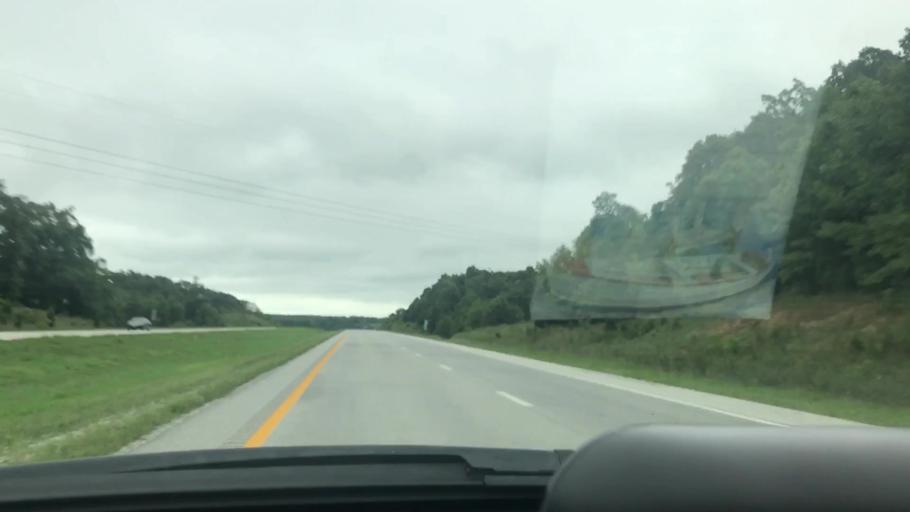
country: US
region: Missouri
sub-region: Greene County
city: Strafford
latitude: 37.2854
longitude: -93.1936
